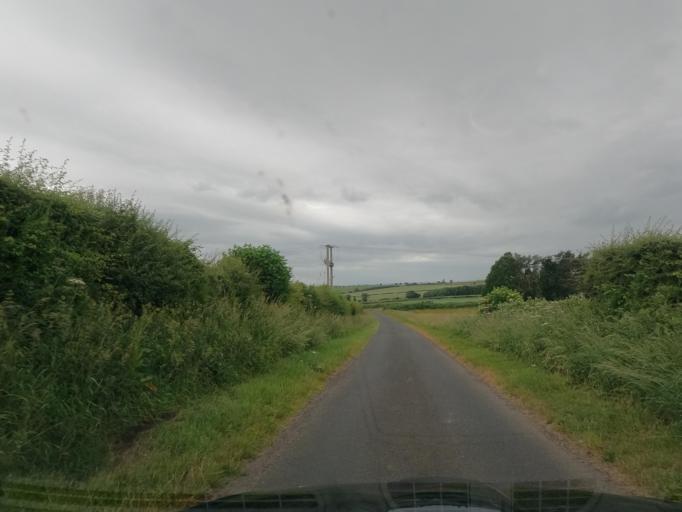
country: GB
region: England
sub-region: Northumberland
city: Ford
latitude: 55.6670
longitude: -2.0943
